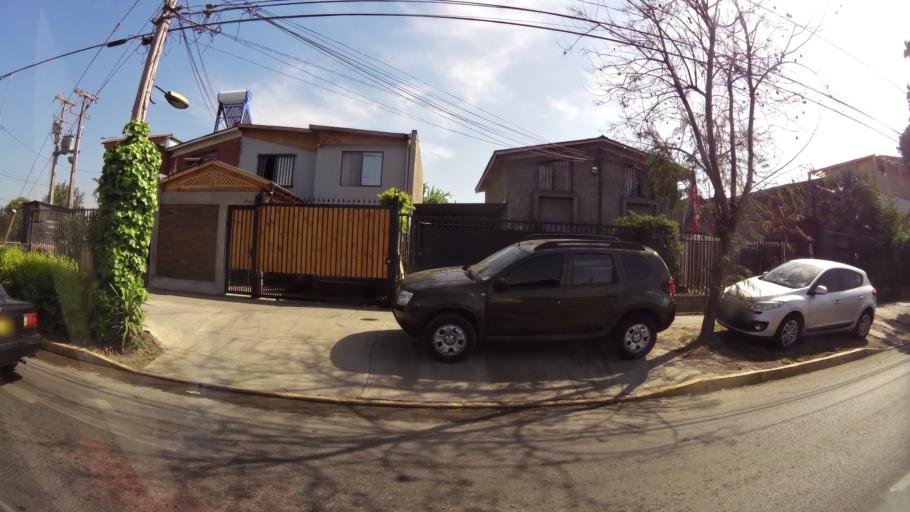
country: CL
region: Santiago Metropolitan
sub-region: Provincia de Santiago
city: Lo Prado
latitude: -33.4823
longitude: -70.7379
